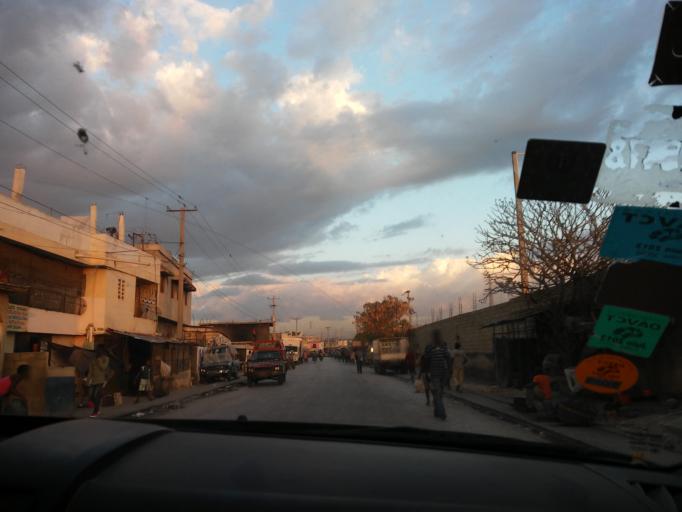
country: HT
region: Ouest
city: Port-au-Prince
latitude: 18.5635
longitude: -72.3432
